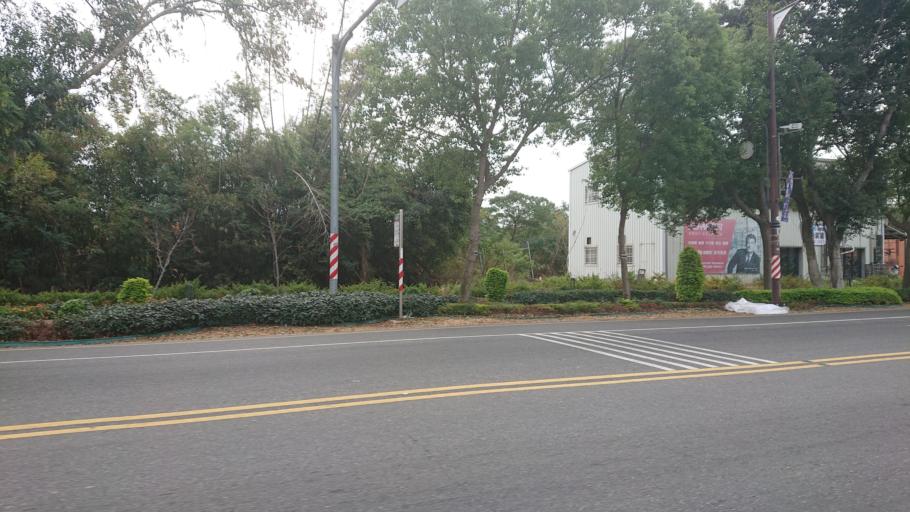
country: TW
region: Fukien
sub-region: Kinmen
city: Jincheng
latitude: 24.4349
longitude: 118.3269
